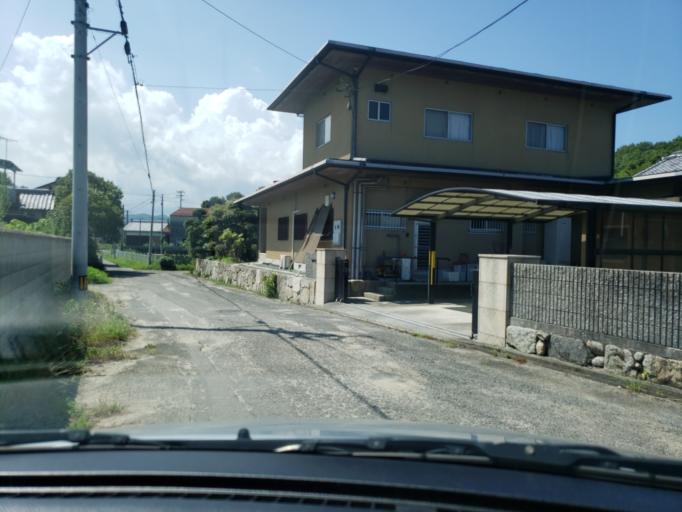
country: JP
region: Ehime
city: Hojo
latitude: 34.0866
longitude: 132.9291
